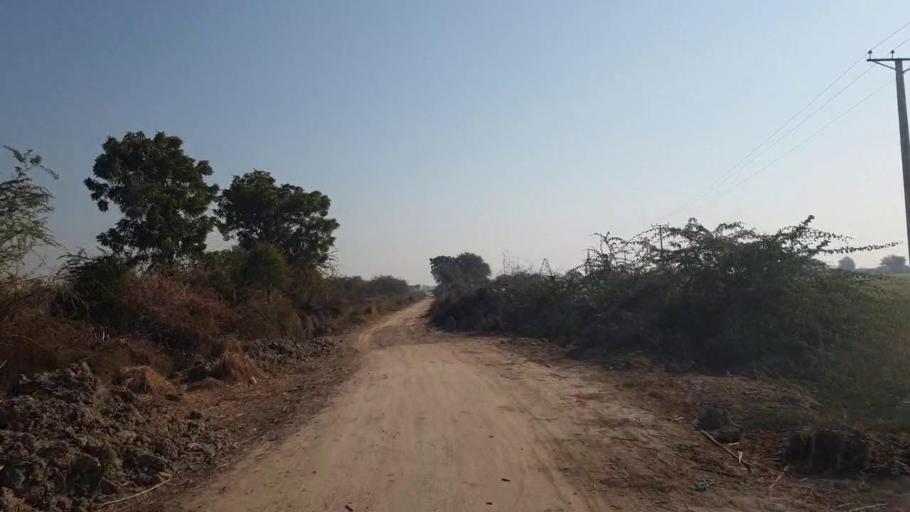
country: PK
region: Sindh
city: Shahpur Chakar
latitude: 26.0662
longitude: 68.6055
